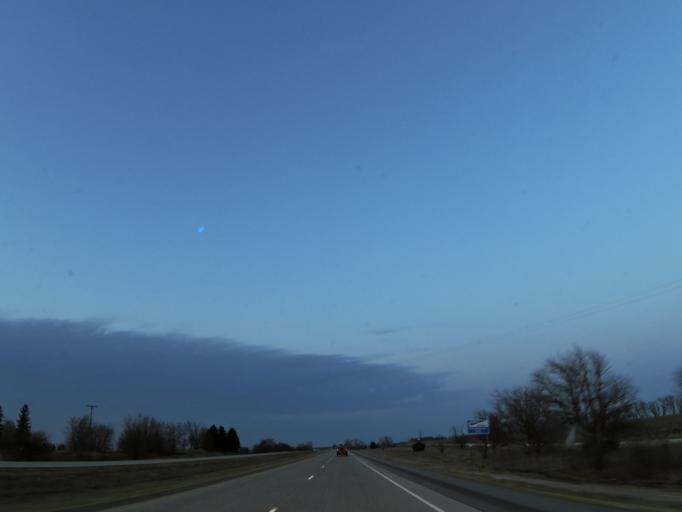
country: US
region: Minnesota
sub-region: Mower County
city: Grand Meadow
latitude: 43.7993
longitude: -92.5954
